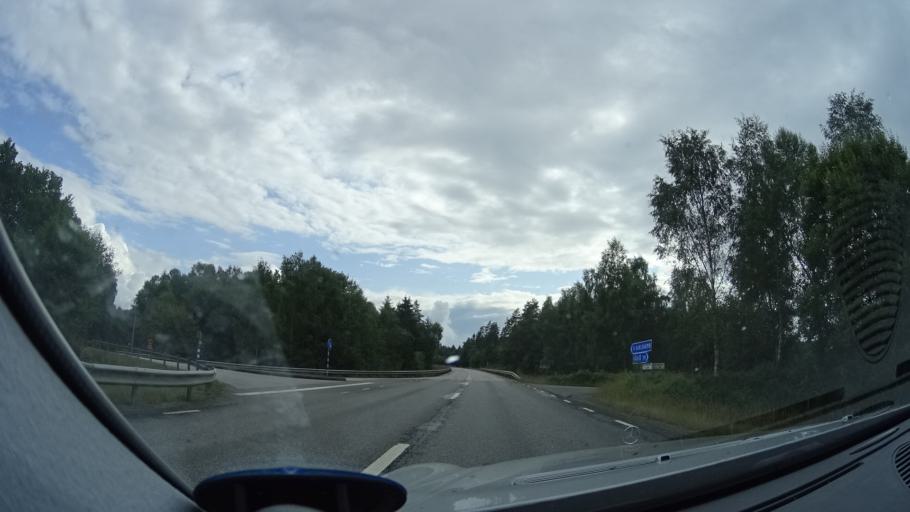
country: SE
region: Blekinge
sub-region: Karlshamns Kommun
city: Svangsta
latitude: 56.2591
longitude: 14.8367
